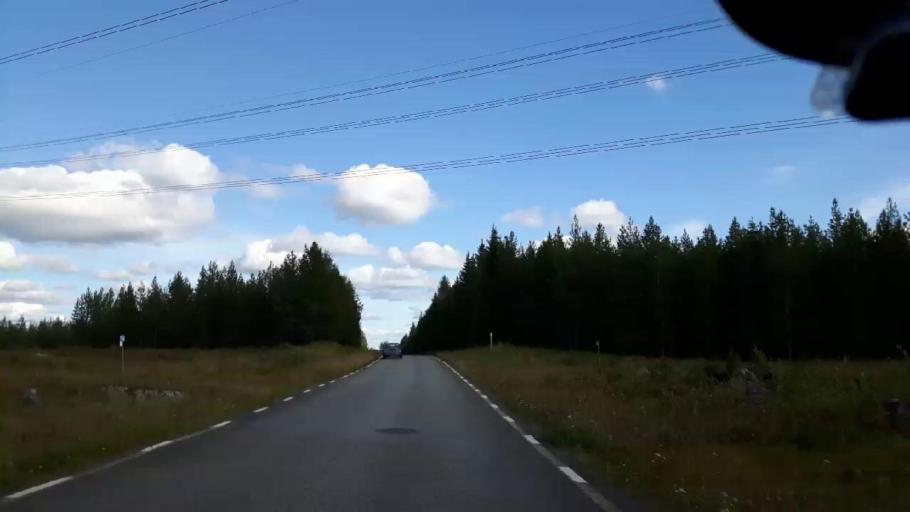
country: SE
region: Jaemtland
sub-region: OEstersunds Kommun
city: Brunflo
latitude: 63.2019
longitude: 15.2298
